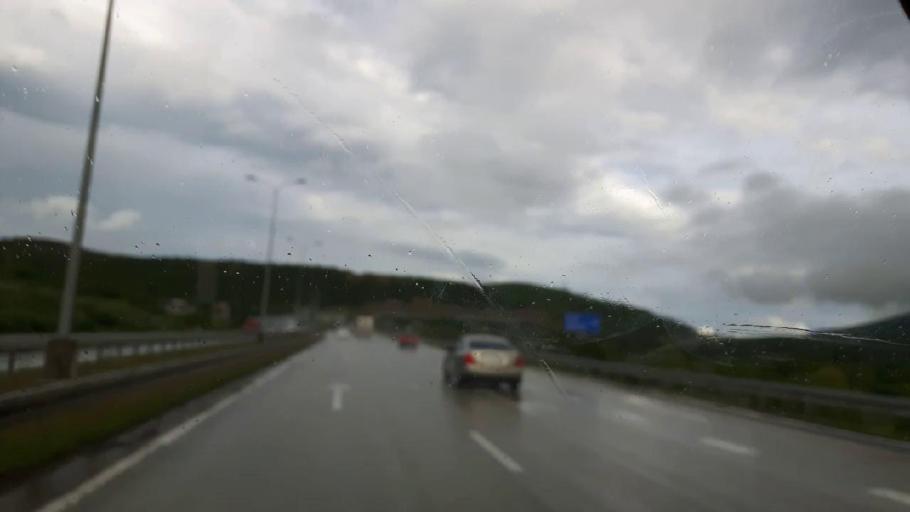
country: GE
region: Shida Kartli
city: Kaspi
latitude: 41.9955
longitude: 44.4135
